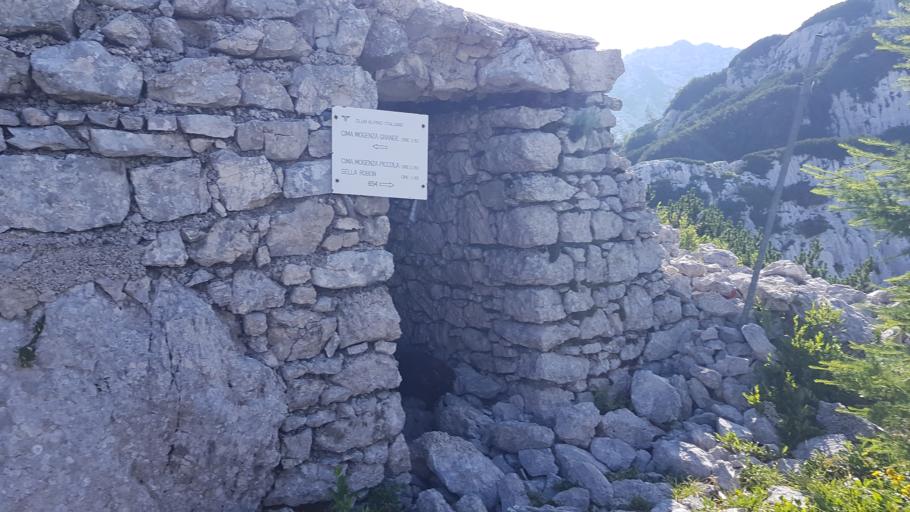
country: SI
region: Bovec
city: Bovec
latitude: 46.3871
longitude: 13.5302
